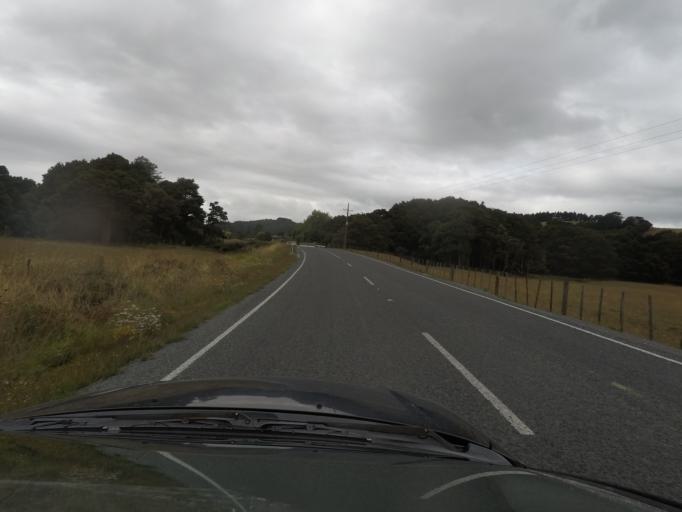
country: NZ
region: Auckland
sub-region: Auckland
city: Wellsford
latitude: -36.2821
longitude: 174.5760
